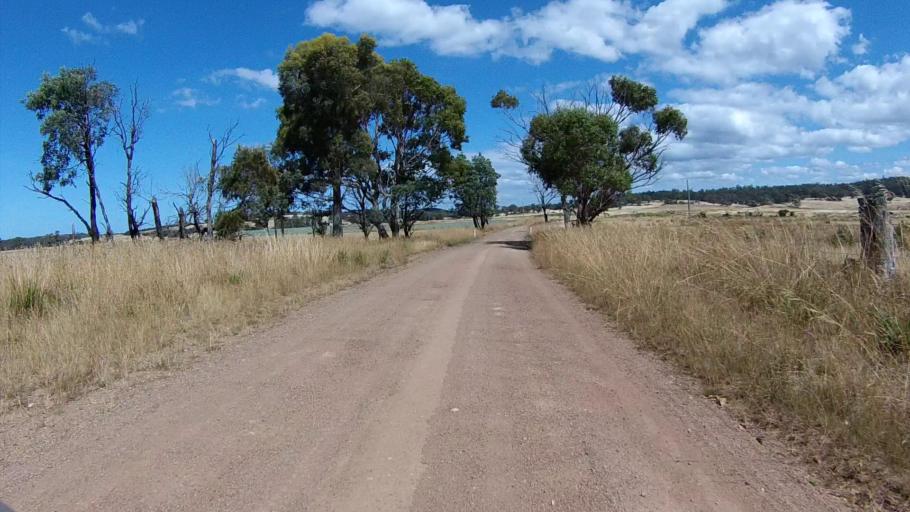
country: AU
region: Tasmania
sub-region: Break O'Day
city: St Helens
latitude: -41.9552
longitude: 148.0699
